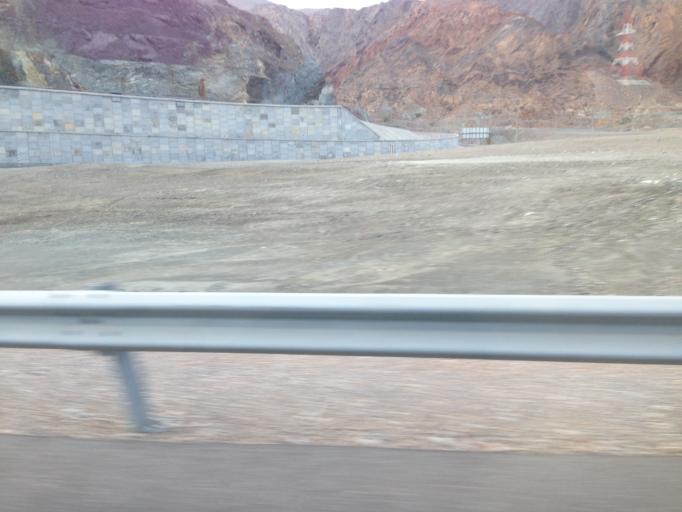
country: OM
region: Muhafazat Masqat
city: Bawshar
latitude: 23.5822
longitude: 58.4462
